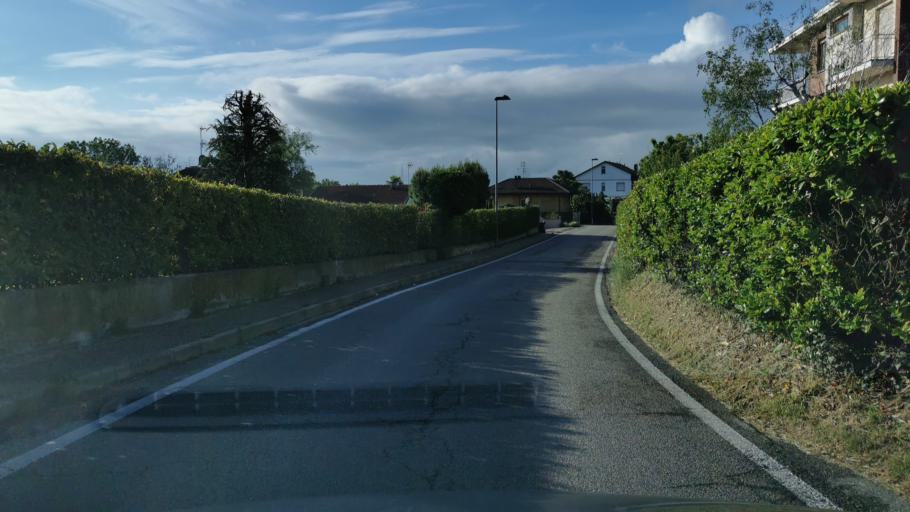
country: IT
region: Piedmont
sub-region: Provincia di Torino
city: Pino Torinese
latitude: 45.0330
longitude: 7.7729
